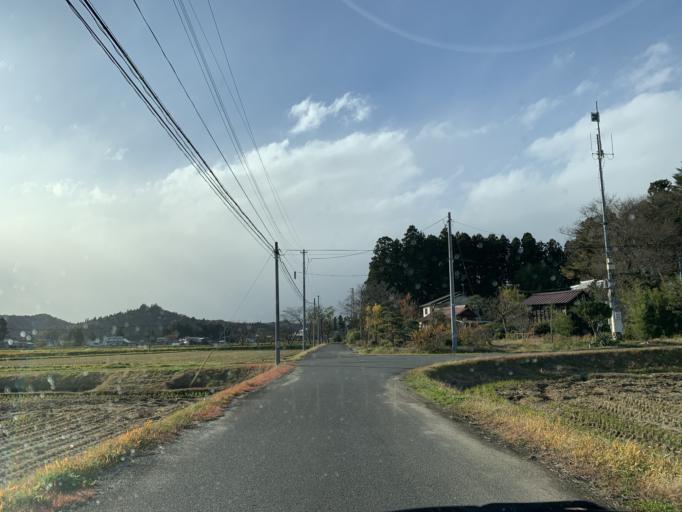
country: JP
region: Iwate
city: Ichinoseki
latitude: 39.0108
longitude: 141.1025
